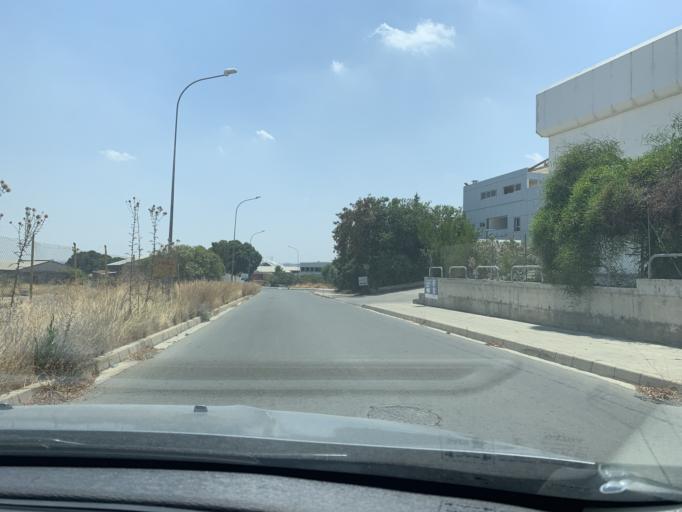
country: CY
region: Lefkosia
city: Nicosia
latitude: 35.1231
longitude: 33.3575
